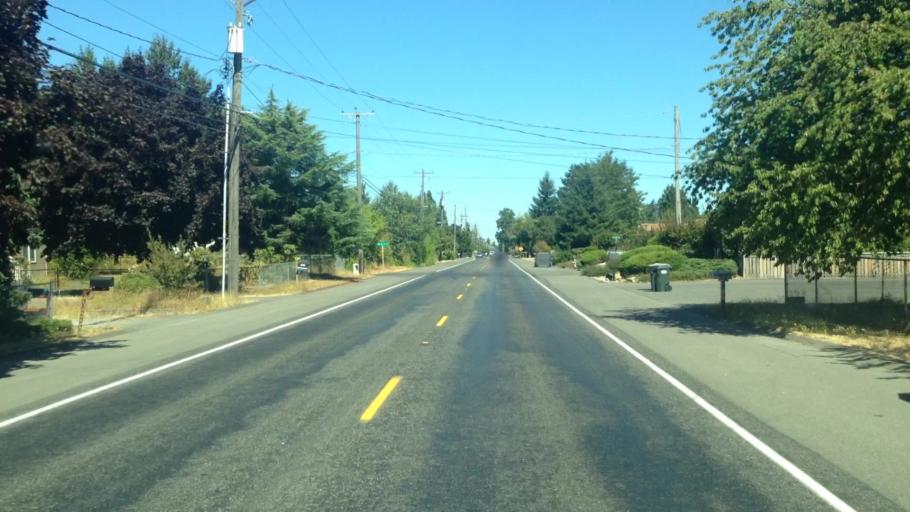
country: US
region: Washington
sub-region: Pierce County
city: Midland
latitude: 47.1642
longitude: -122.4155
